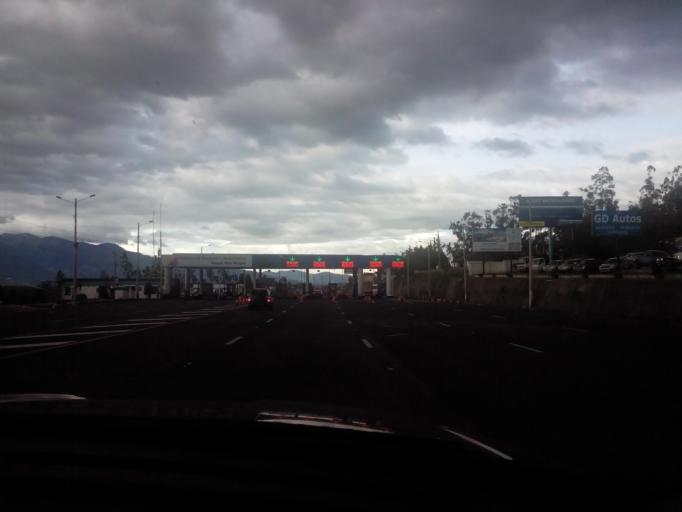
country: EC
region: Imbabura
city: Cotacachi
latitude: 0.2884
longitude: -78.2364
